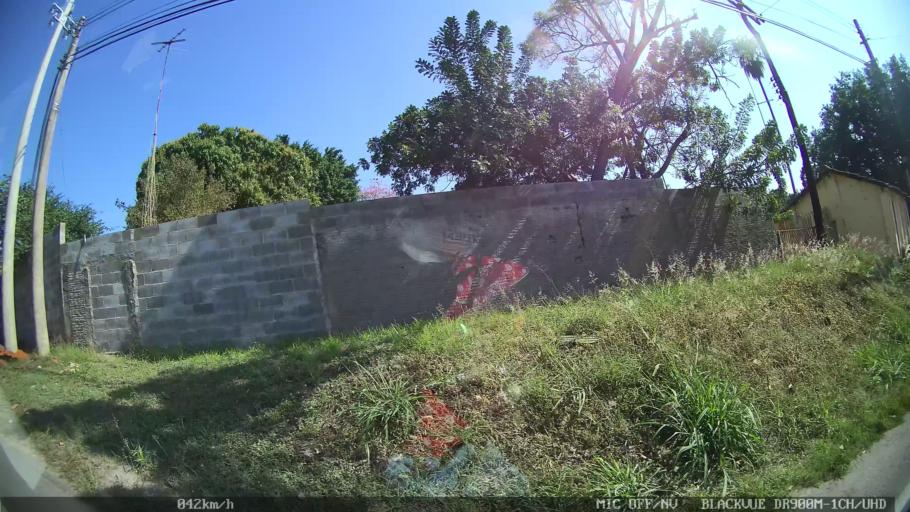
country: BR
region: Sao Paulo
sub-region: Valinhos
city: Valinhos
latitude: -22.9994
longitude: -47.0849
